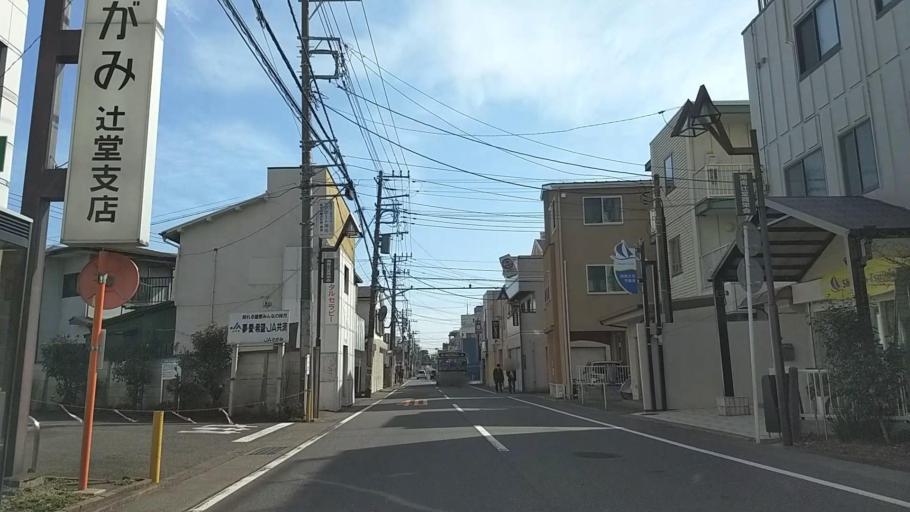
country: JP
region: Kanagawa
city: Fujisawa
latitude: 35.3316
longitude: 139.4511
